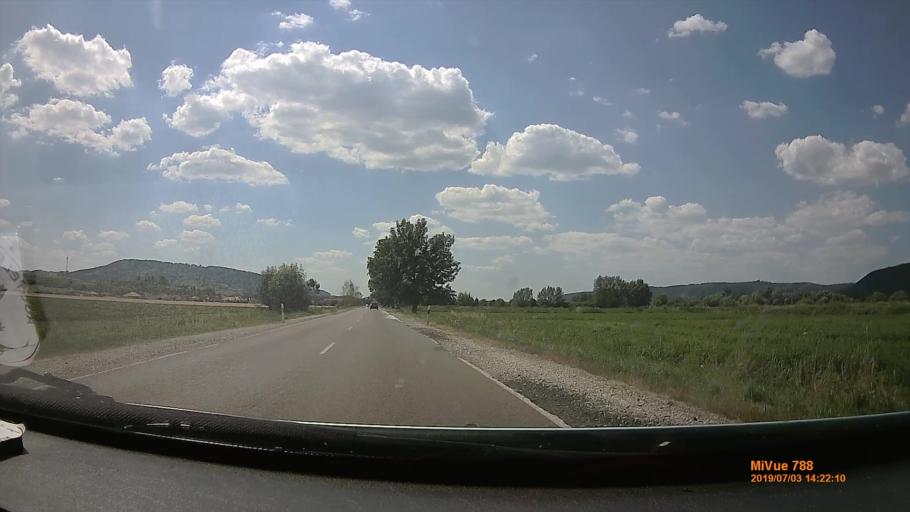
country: HU
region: Borsod-Abauj-Zemplen
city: Sajokaza
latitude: 48.2741
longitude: 20.5682
